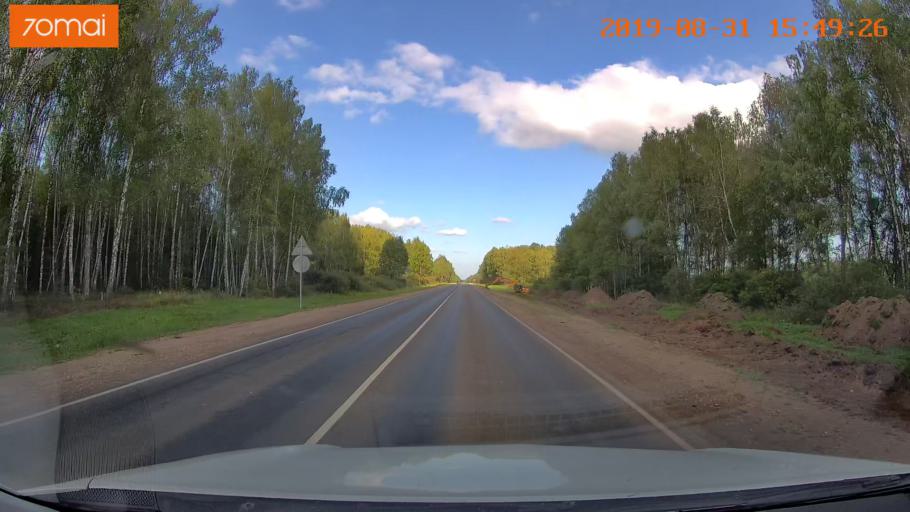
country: RU
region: Kaluga
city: Yukhnov
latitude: 54.6909
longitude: 35.0502
